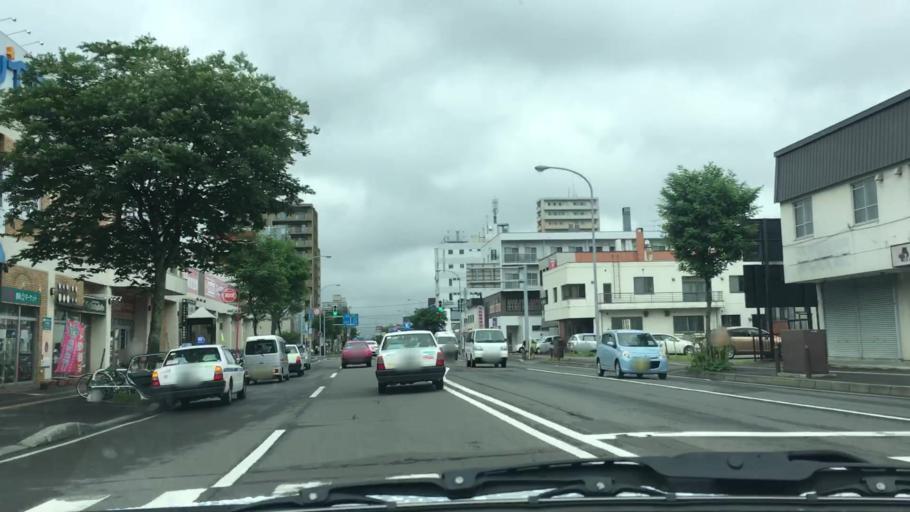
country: JP
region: Hokkaido
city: Sapporo
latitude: 43.0783
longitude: 141.3644
